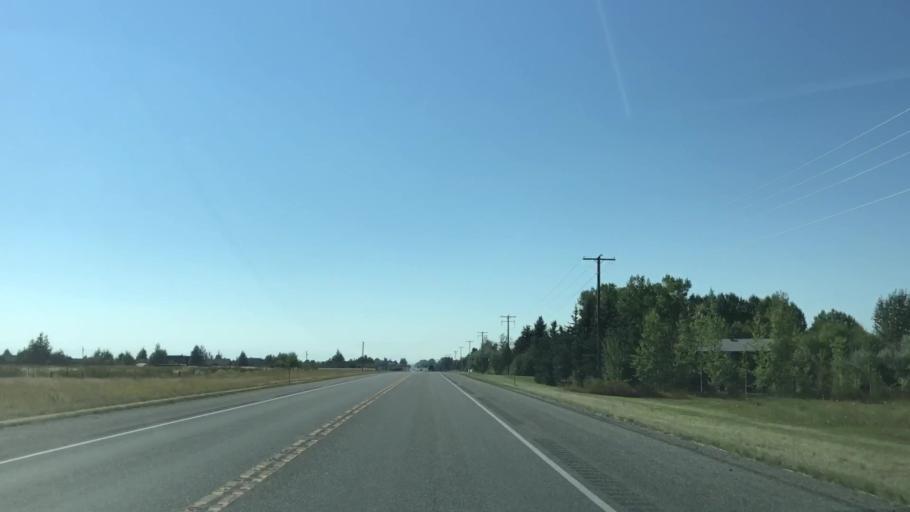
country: US
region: Montana
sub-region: Gallatin County
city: Belgrade
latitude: 45.7293
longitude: -111.1180
